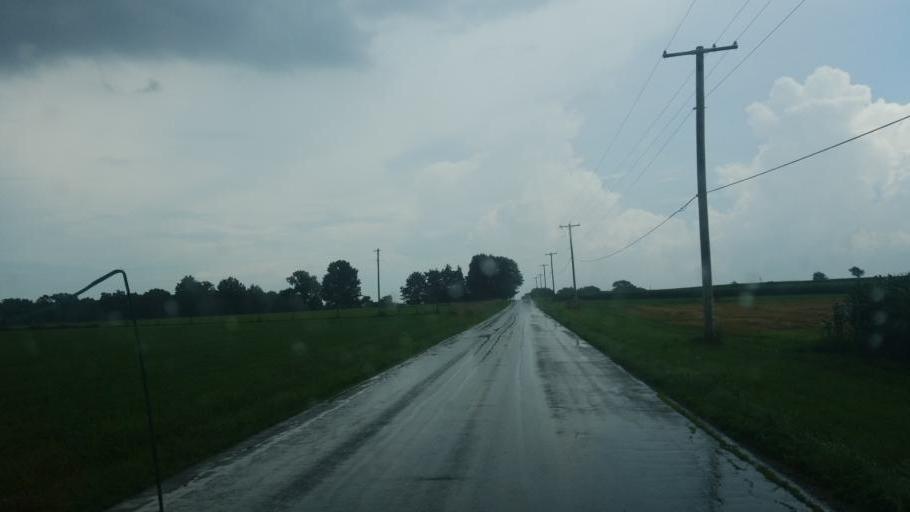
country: US
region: Ohio
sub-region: Wayne County
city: Orrville
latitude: 40.9019
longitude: -81.7989
